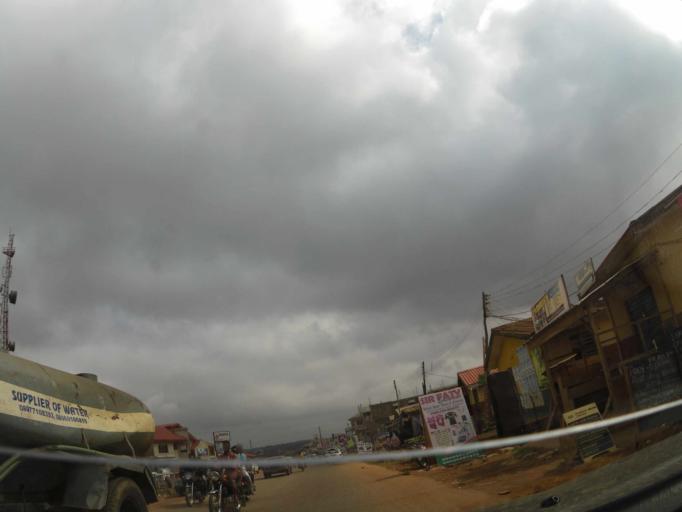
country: NG
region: Oyo
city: Ibadan
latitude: 7.4418
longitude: 3.9514
